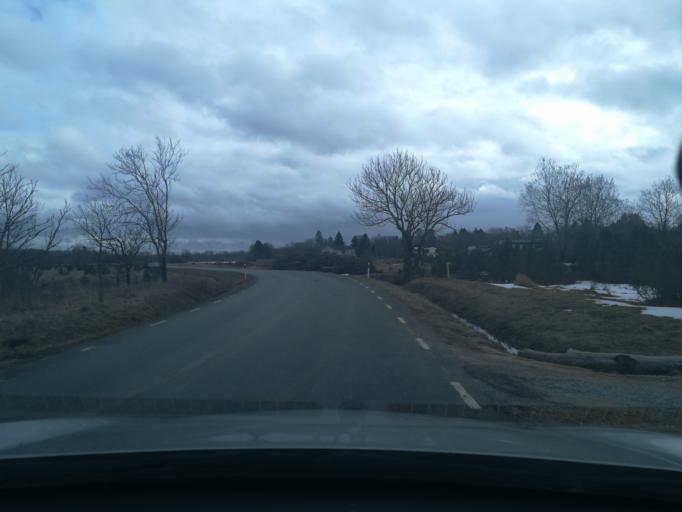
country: EE
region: Harju
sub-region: Saue linn
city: Saue
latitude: 59.3588
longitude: 24.5269
